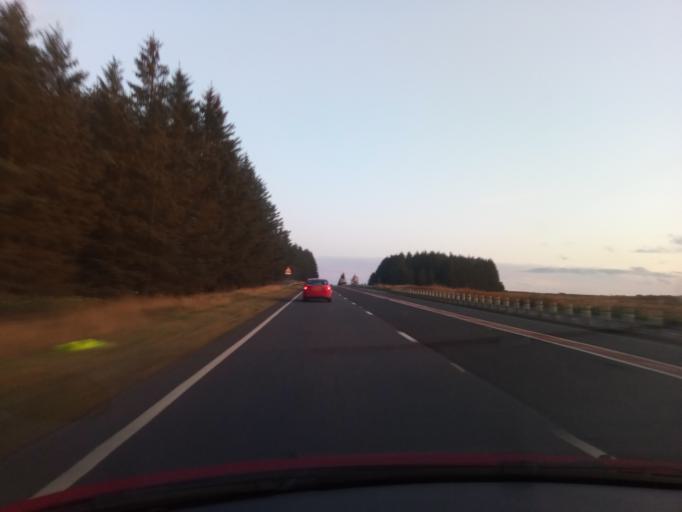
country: GB
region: Scotland
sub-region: East Lothian
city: Pencaitland
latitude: 55.8103
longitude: -2.8398
